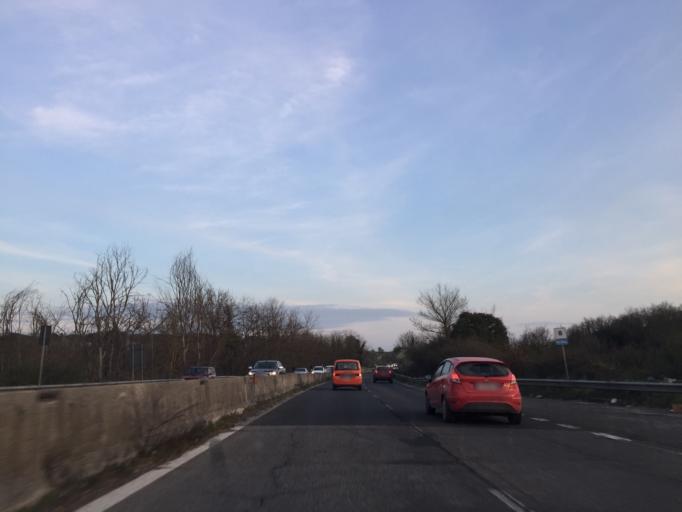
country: IT
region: Latium
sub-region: Citta metropolitana di Roma Capitale
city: Formello
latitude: 42.0408
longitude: 12.4212
